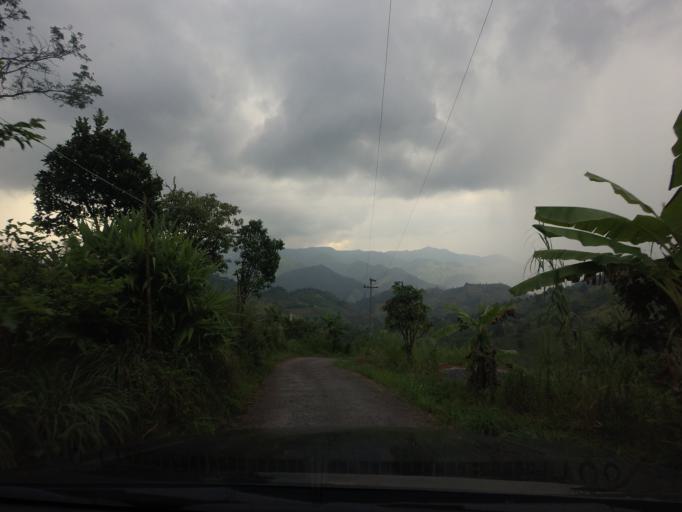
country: TH
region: Nan
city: Bo Kluea
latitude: 19.3507
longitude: 101.1780
